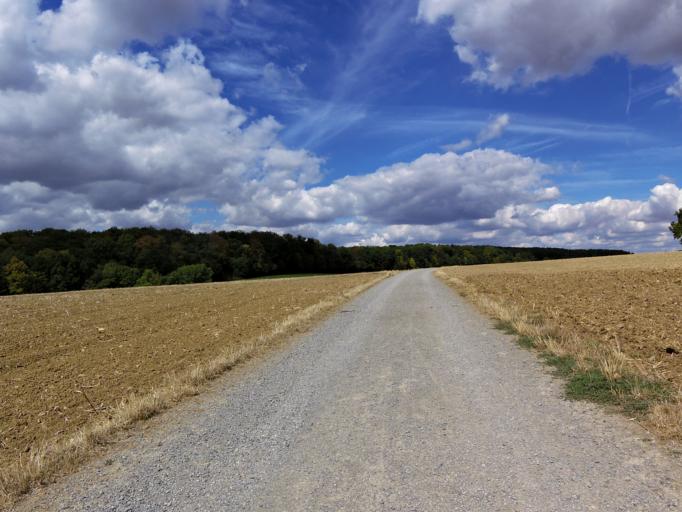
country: DE
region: Bavaria
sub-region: Regierungsbezirk Unterfranken
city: Gadheim
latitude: 49.8452
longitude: 9.8980
